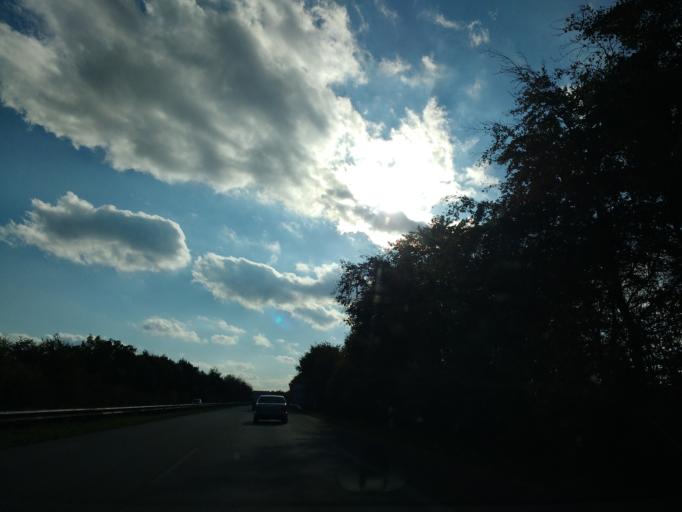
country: DE
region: Schleswig-Holstein
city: Travemuende
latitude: 53.9407
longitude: 10.8343
